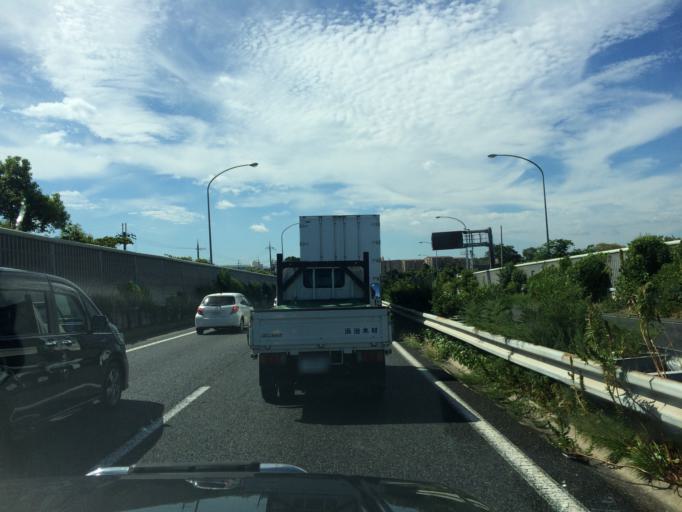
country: JP
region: Osaka
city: Takaishi
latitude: 34.5025
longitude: 135.4881
